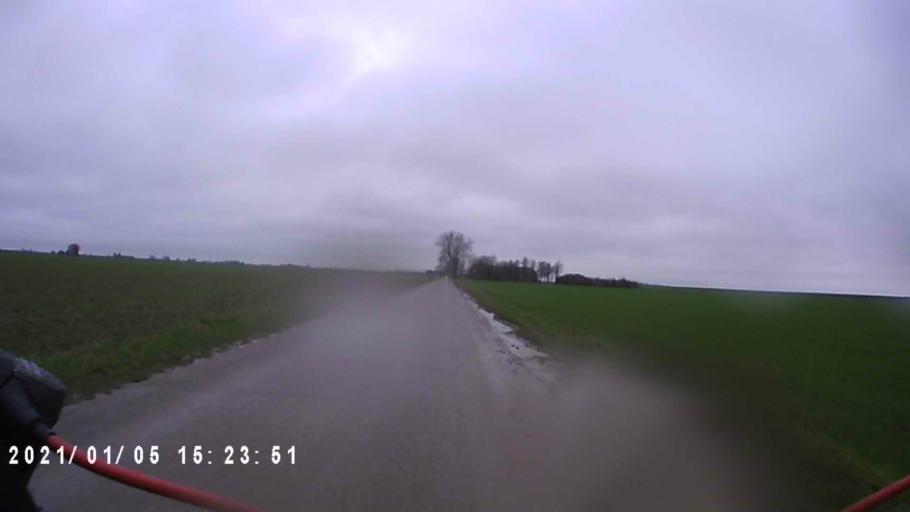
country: DE
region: Lower Saxony
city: Bunde
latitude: 53.2280
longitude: 7.2050
